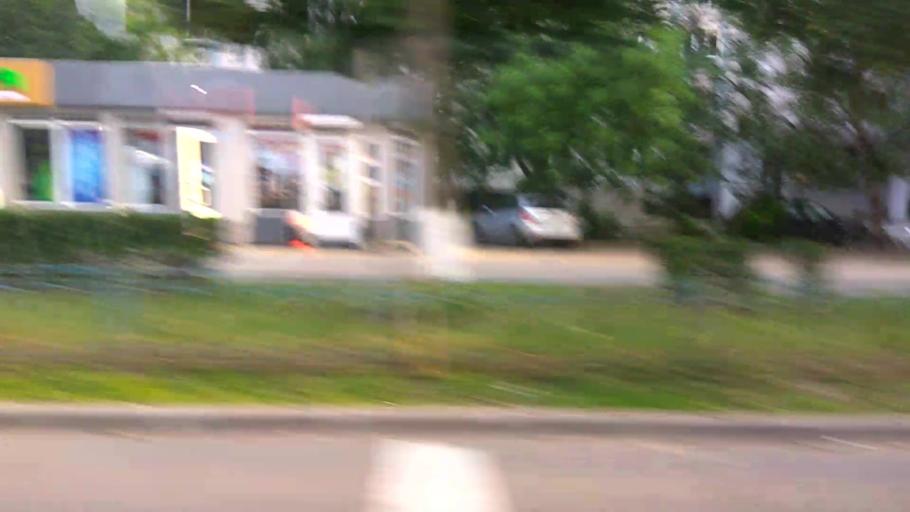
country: RU
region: Moskovskaya
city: Yubileyny
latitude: 55.9229
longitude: 37.8646
